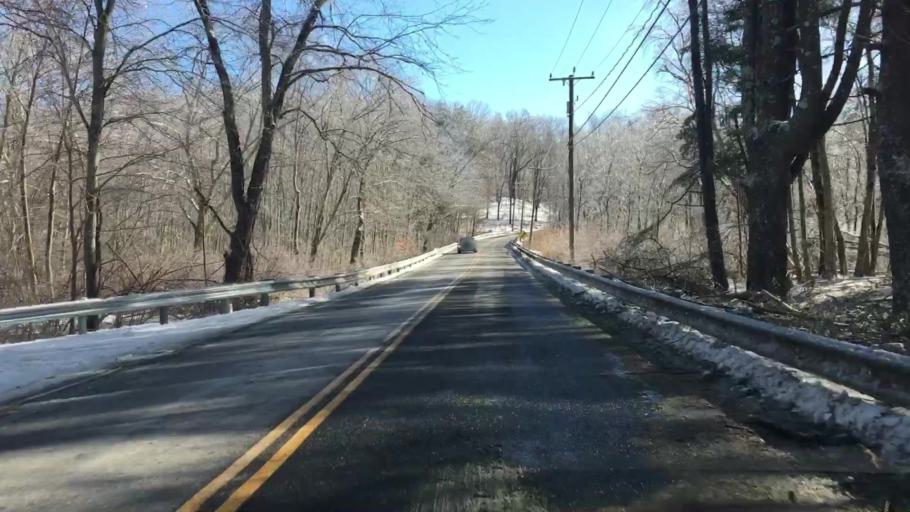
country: US
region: Connecticut
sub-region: Fairfield County
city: Newtown
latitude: 41.3590
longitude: -73.2382
